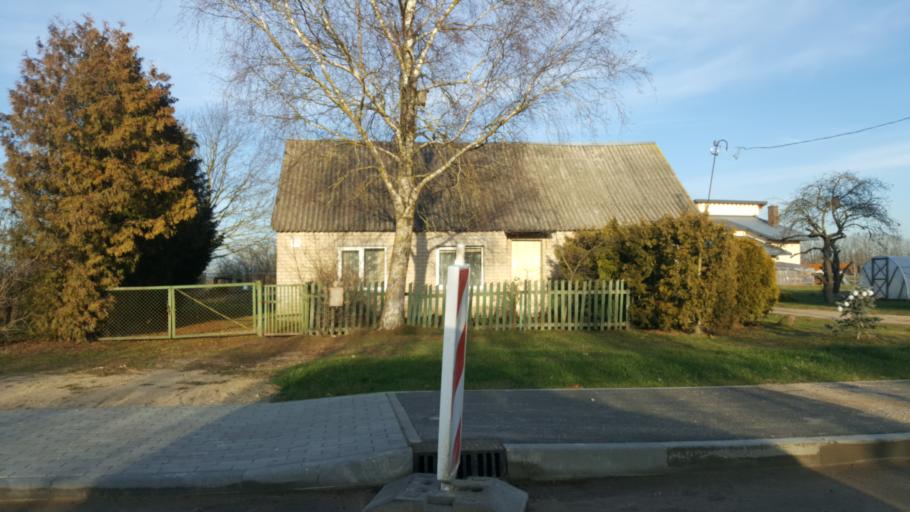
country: LT
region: Kauno apskritis
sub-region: Kauno rajonas
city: Mastaiciai
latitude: 54.8559
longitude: 23.8519
